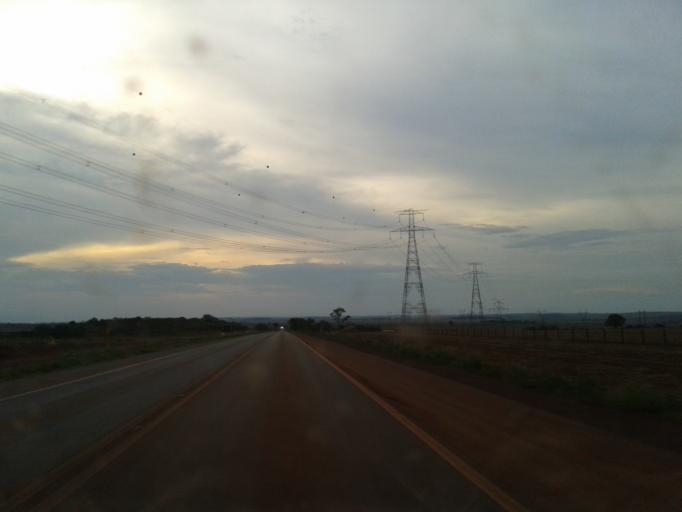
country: BR
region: Goias
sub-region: Santa Helena De Goias
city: Santa Helena de Goias
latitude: -17.9060
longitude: -50.6317
